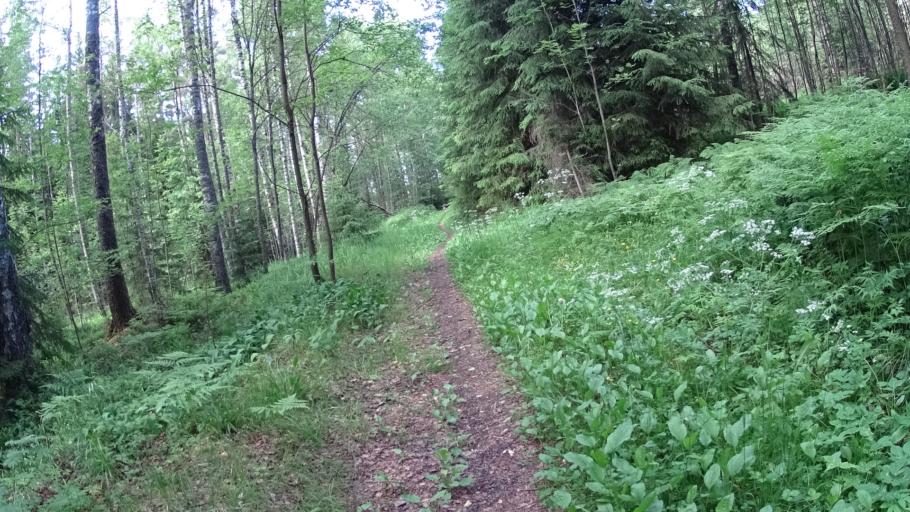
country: FI
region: Uusimaa
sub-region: Helsinki
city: Kilo
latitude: 60.2846
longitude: 24.8037
